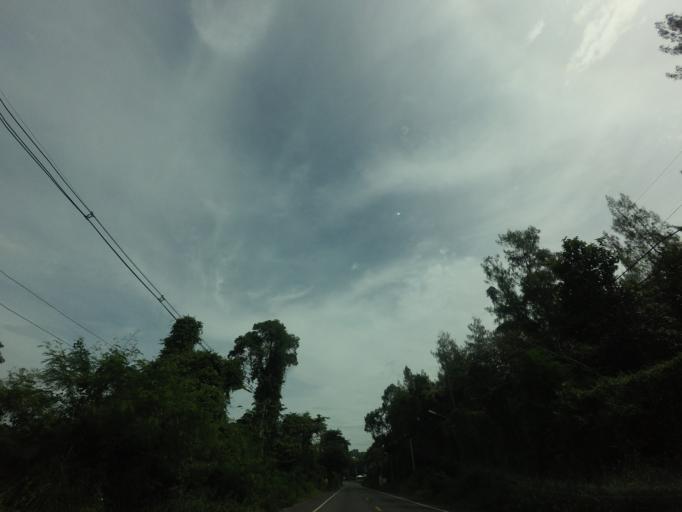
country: TH
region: Rayong
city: Klaeng
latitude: 12.6338
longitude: 101.5576
